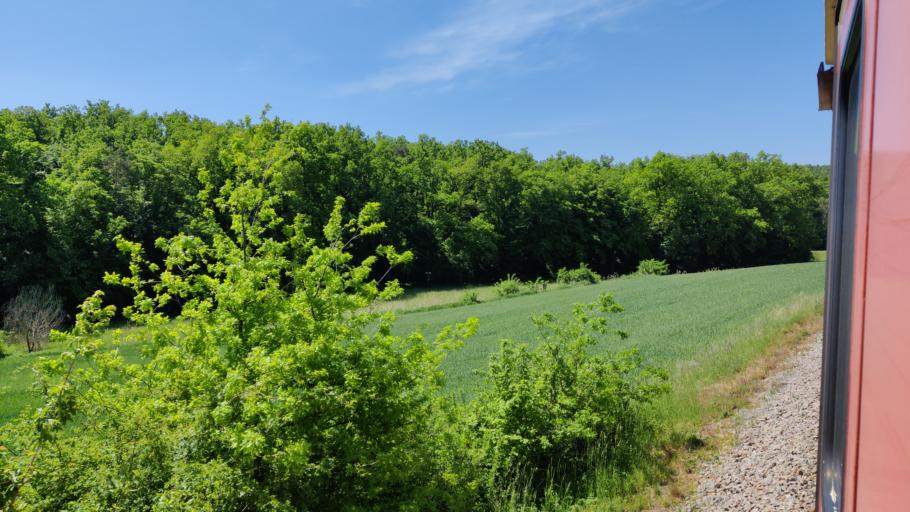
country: AT
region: Lower Austria
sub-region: Politischer Bezirk Horn
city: Horn
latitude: 48.6343
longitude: 15.6776
